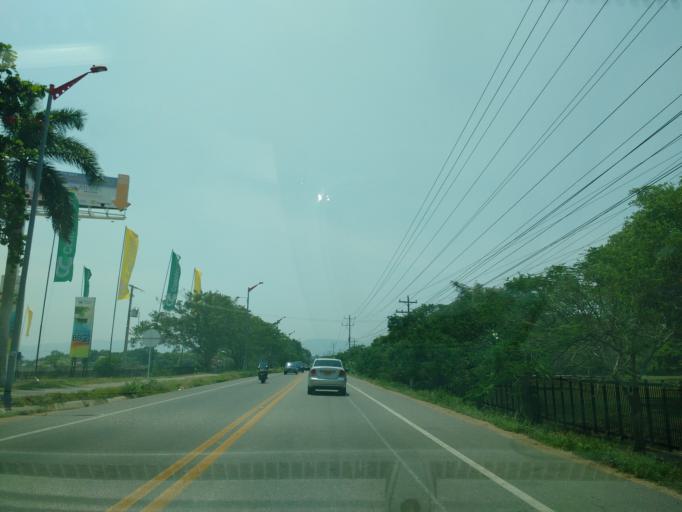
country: CO
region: Cundinamarca
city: Ricaurte
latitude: 4.2822
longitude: -74.7681
